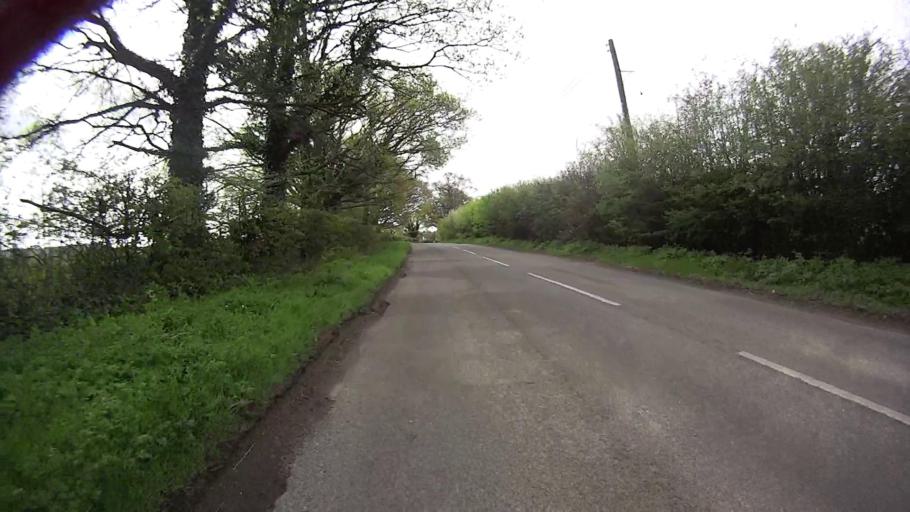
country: GB
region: England
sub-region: Surrey
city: Newdigate
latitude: 51.1143
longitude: -0.2900
